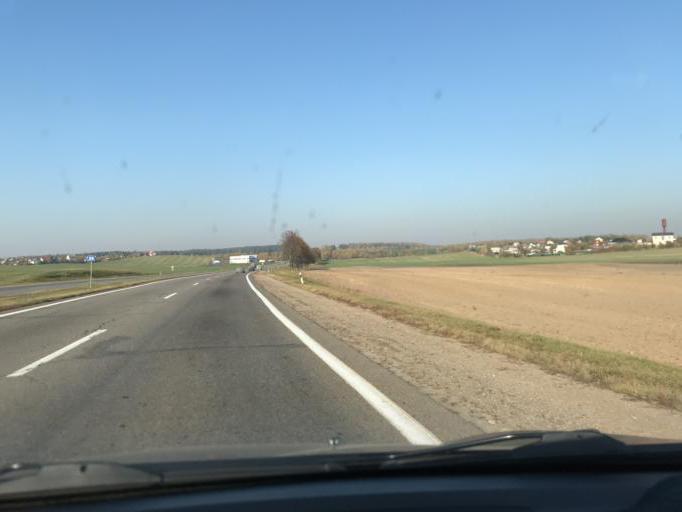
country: BY
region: Minsk
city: Luhavaya Slabada
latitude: 53.7498
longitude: 27.8339
